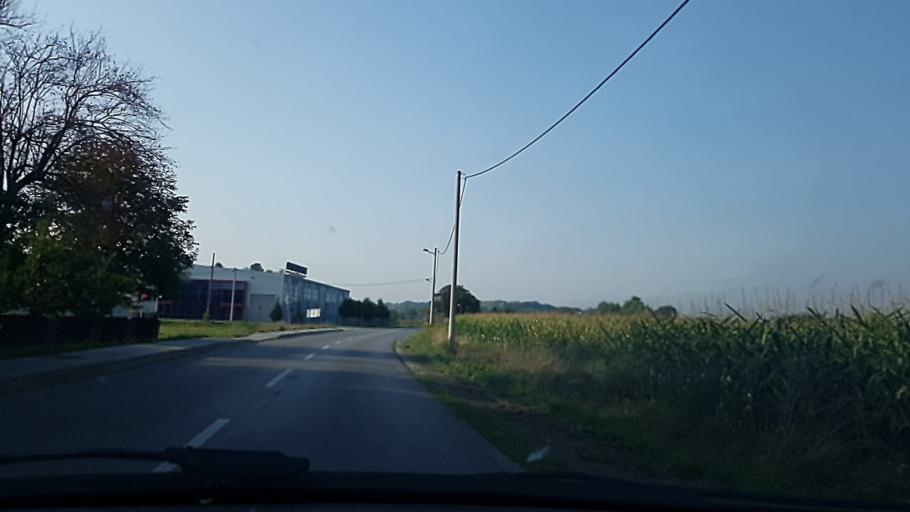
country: HR
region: Zagrebacka
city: Pojatno
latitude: 45.9393
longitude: 15.8123
